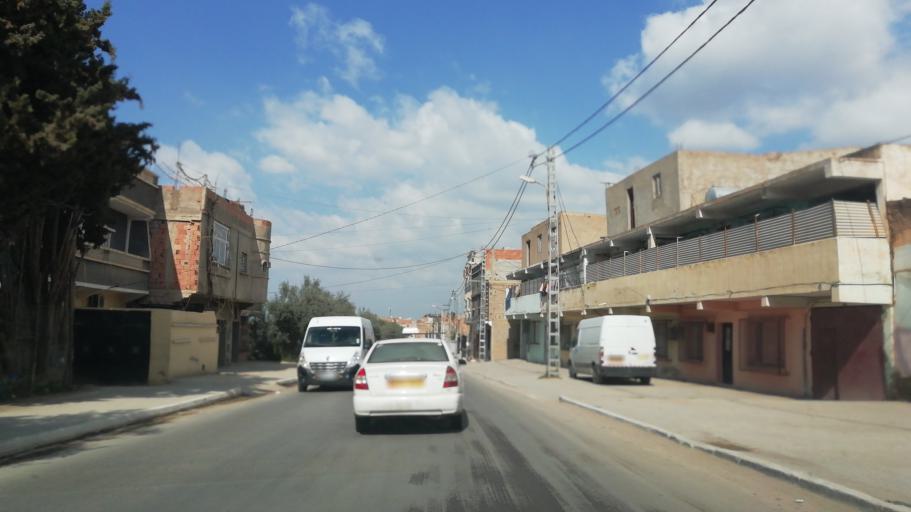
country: DZ
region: Mascara
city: Mascara
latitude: 35.5746
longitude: 0.0700
